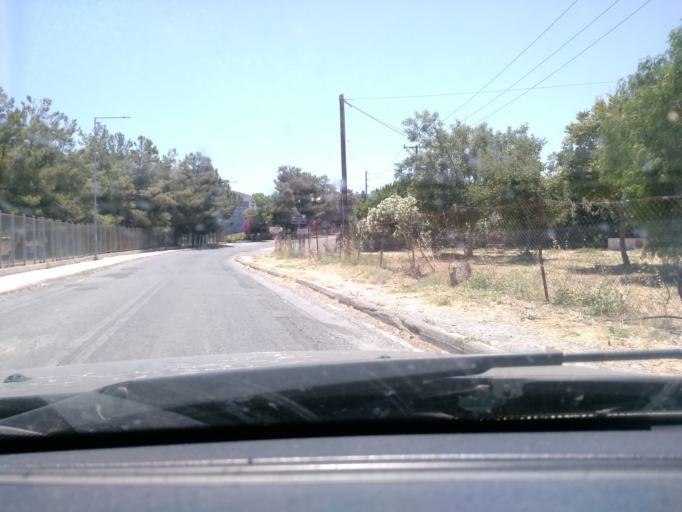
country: GR
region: Crete
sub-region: Nomos Irakleiou
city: Gazi
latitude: 35.3169
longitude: 25.1014
